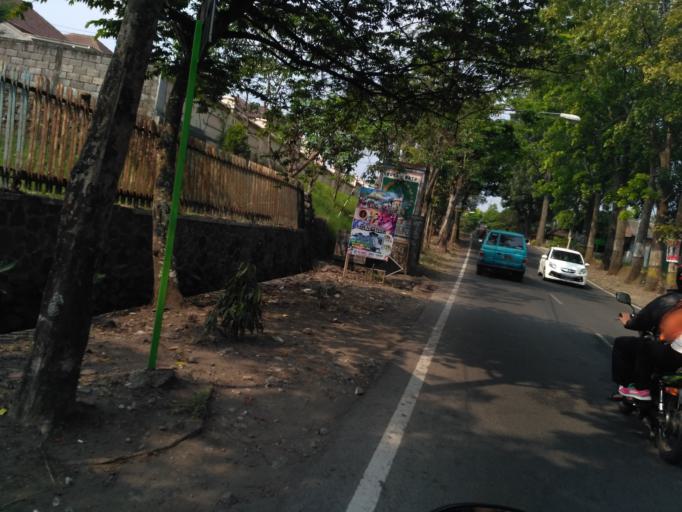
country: ID
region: East Java
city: Batu
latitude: -7.8634
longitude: 112.5330
